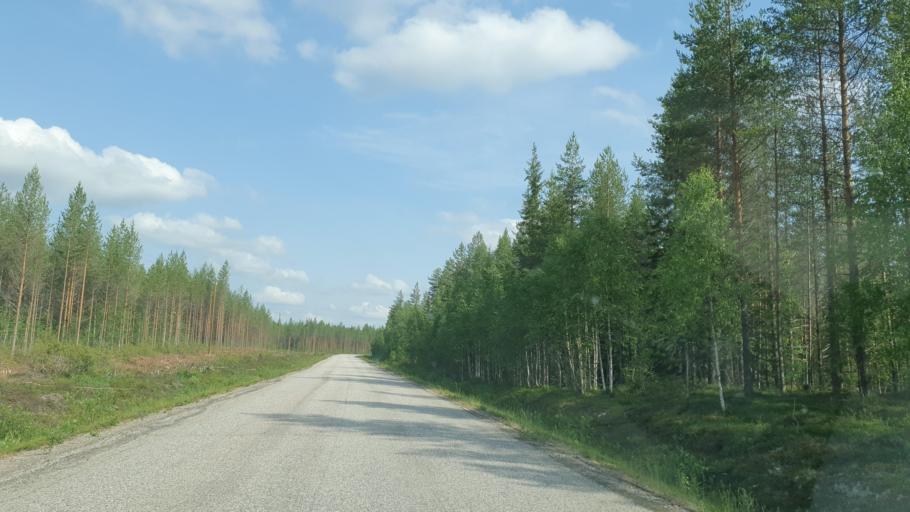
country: FI
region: Kainuu
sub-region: Kehys-Kainuu
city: Kuhmo
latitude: 64.0543
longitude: 29.8891
